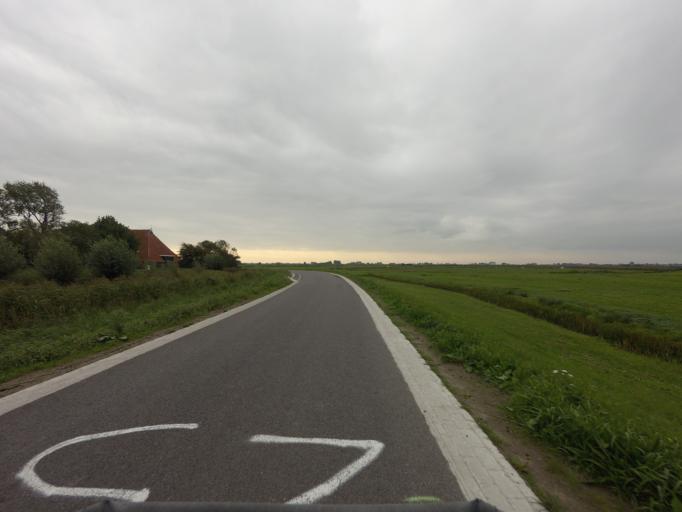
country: NL
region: Friesland
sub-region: Sudwest Fryslan
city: IJlst
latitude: 53.0113
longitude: 5.5746
